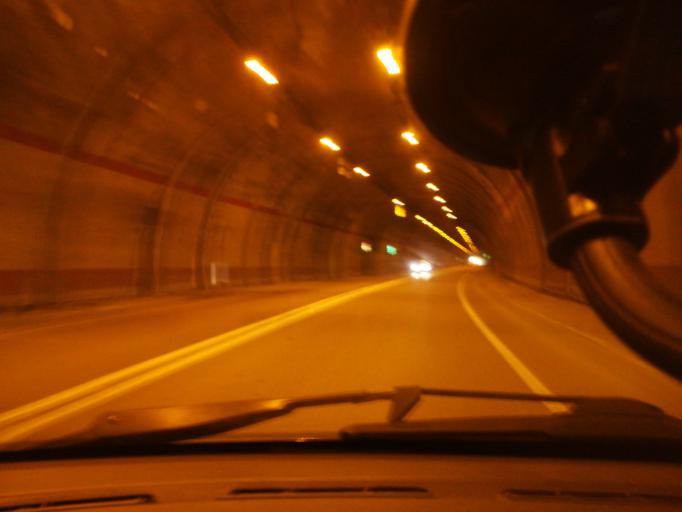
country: IT
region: The Marches
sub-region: Provincia di Macerata
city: Macerata
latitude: 43.3032
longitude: 13.4432
